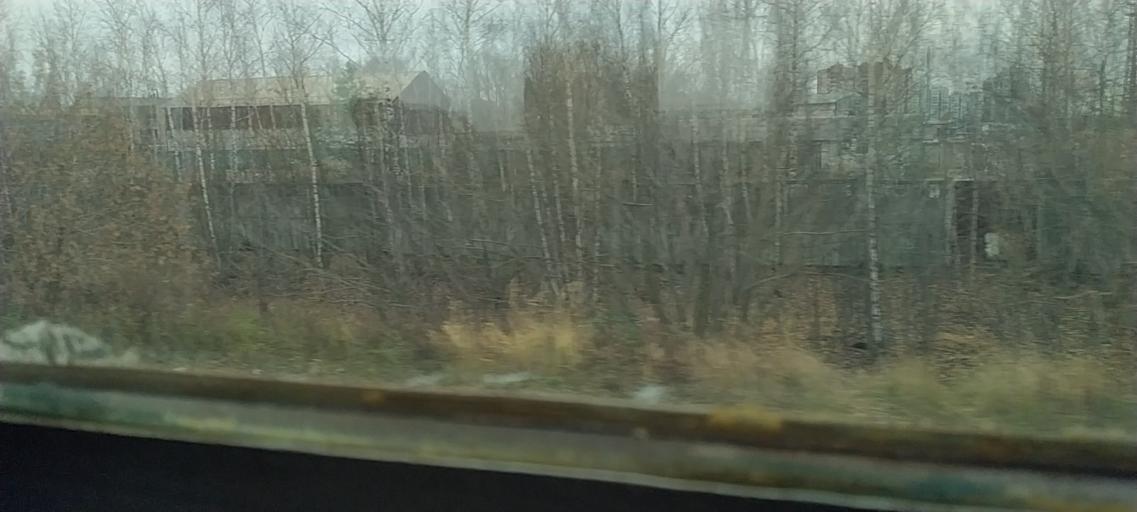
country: RU
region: Moskovskaya
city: Kraskovo
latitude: 55.6692
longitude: 37.9772
